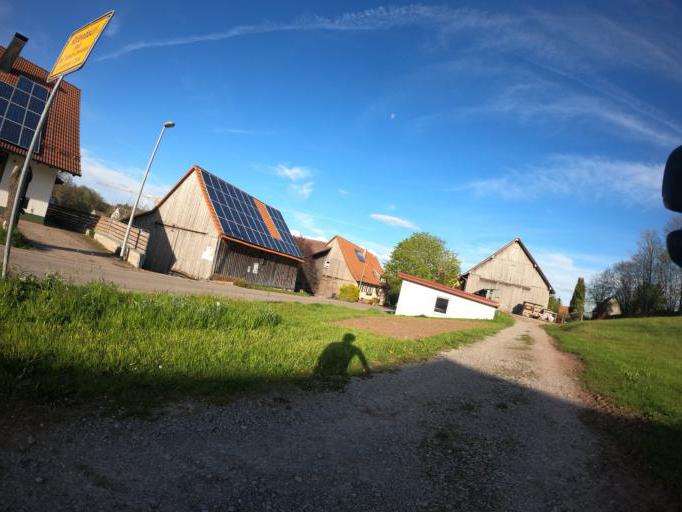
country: DE
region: Baden-Wuerttemberg
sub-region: Karlsruhe Region
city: Oberreichenbach
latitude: 48.7098
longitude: 8.6619
